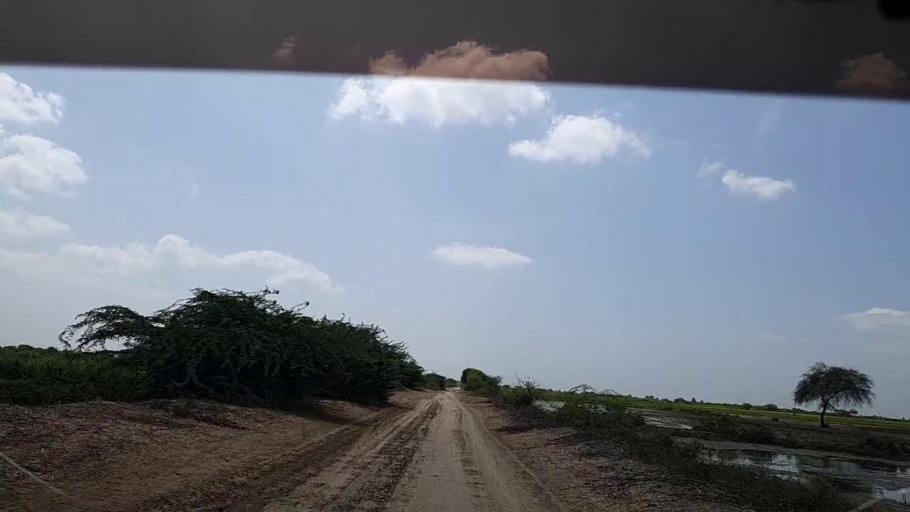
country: PK
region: Sindh
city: Badin
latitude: 24.5587
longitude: 68.7426
